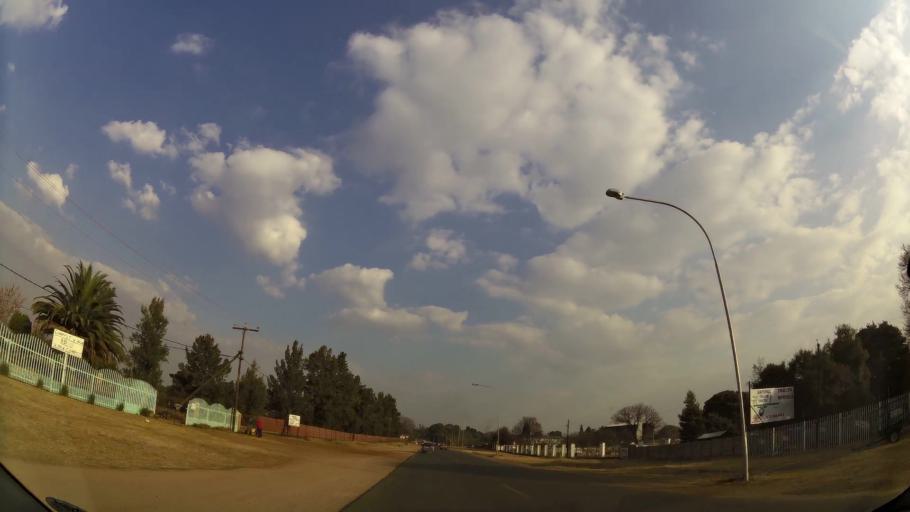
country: ZA
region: Gauteng
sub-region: Ekurhuleni Metropolitan Municipality
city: Benoni
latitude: -26.1185
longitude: 28.2943
